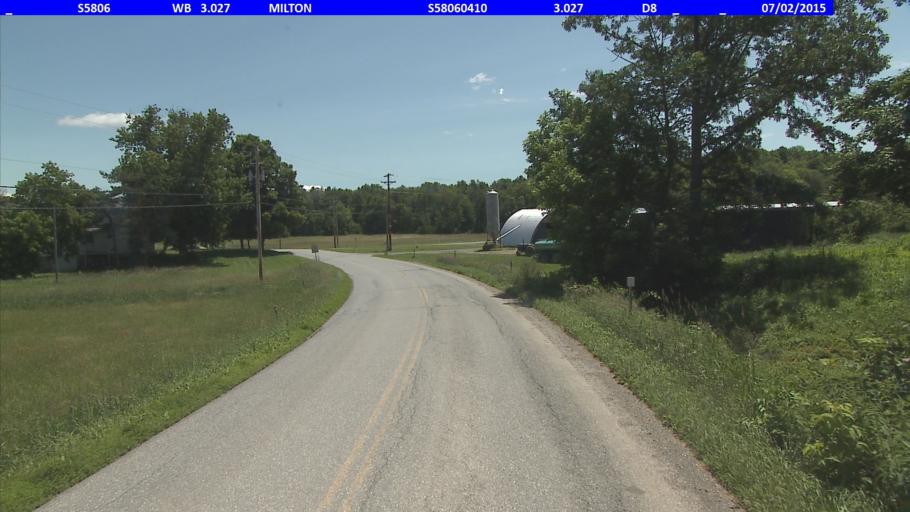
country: US
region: Vermont
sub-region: Chittenden County
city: Milton
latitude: 44.6682
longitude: -73.1679
